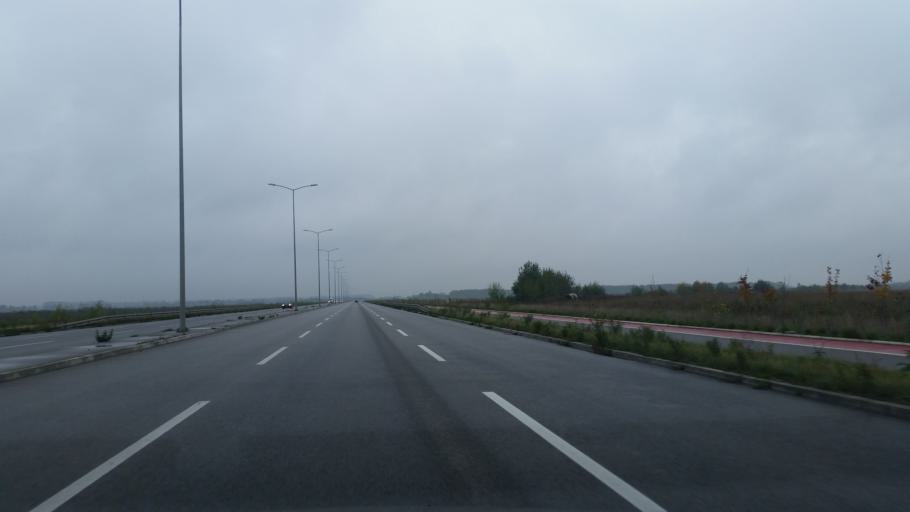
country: RS
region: Central Serbia
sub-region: Belgrade
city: Zemun
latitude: 44.8780
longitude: 20.3932
